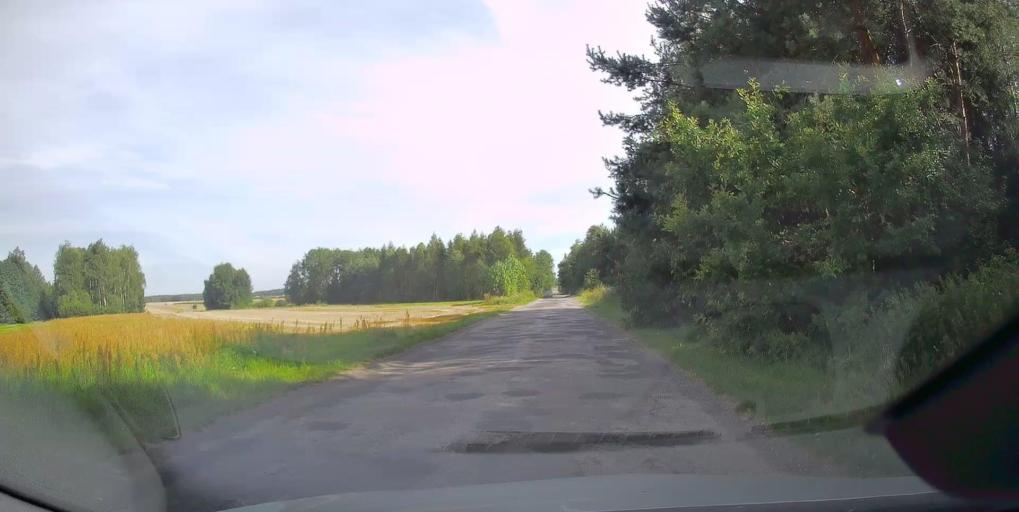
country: PL
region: Lodz Voivodeship
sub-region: Powiat opoczynski
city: Mniszkow
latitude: 51.4195
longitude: 20.0284
